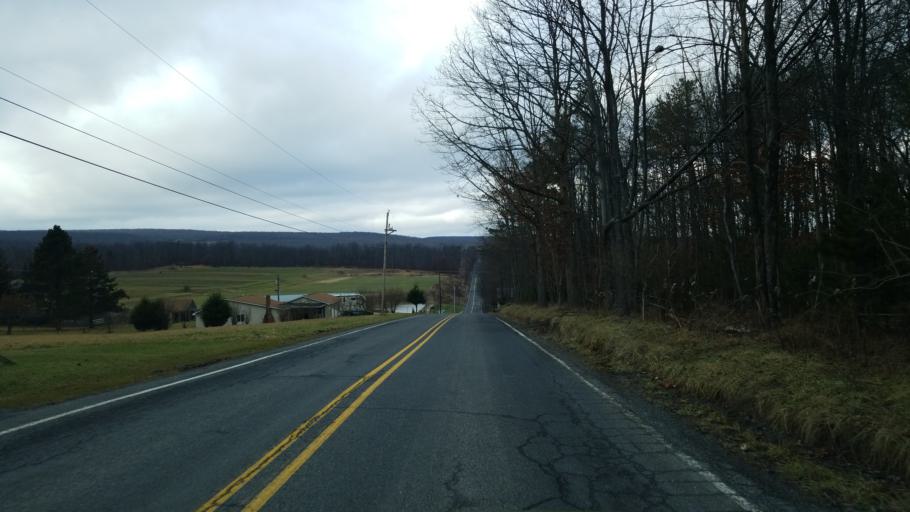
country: US
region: Pennsylvania
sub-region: Clearfield County
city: Hyde
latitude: 41.0412
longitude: -78.4892
